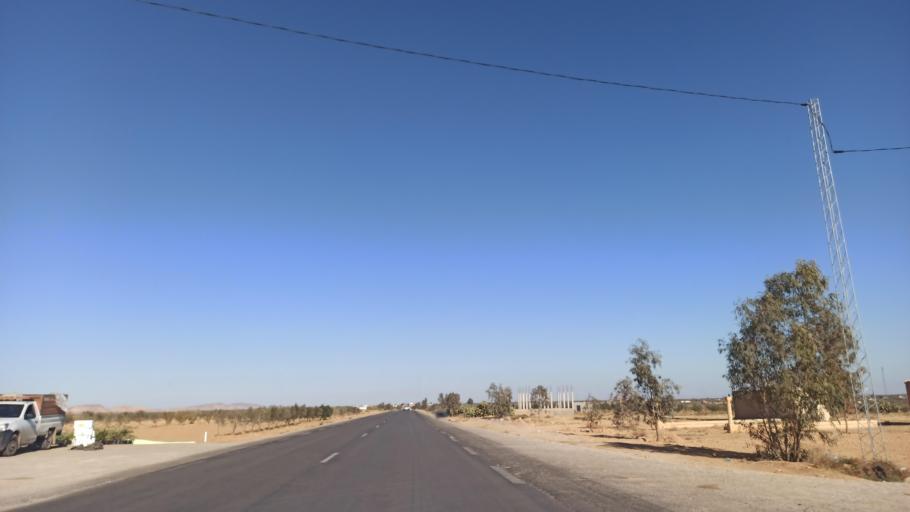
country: TN
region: Sidi Bu Zayd
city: Bi'r al Hufayy
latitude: 34.9522
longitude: 9.2132
